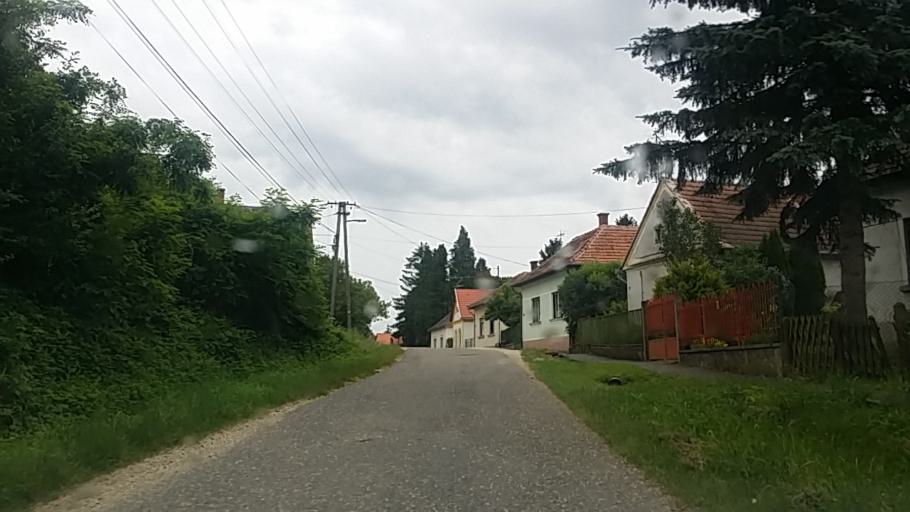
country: HU
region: Zala
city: Zalalovo
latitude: 46.8683
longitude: 16.5426
